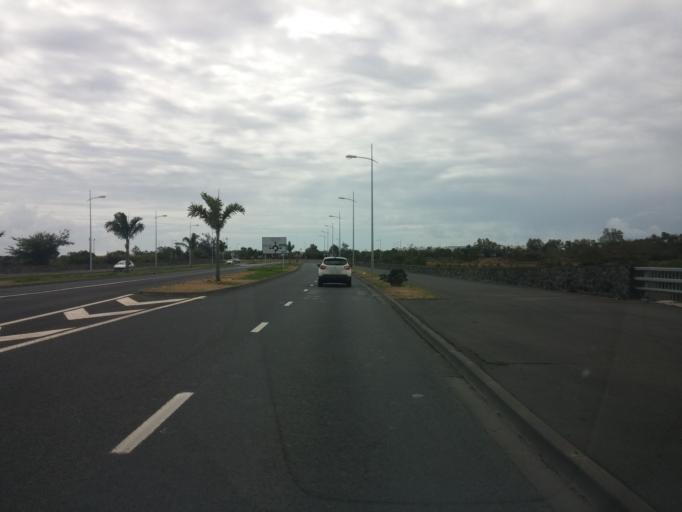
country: RE
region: Reunion
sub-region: Reunion
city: Le Port
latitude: -20.9551
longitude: 55.2943
